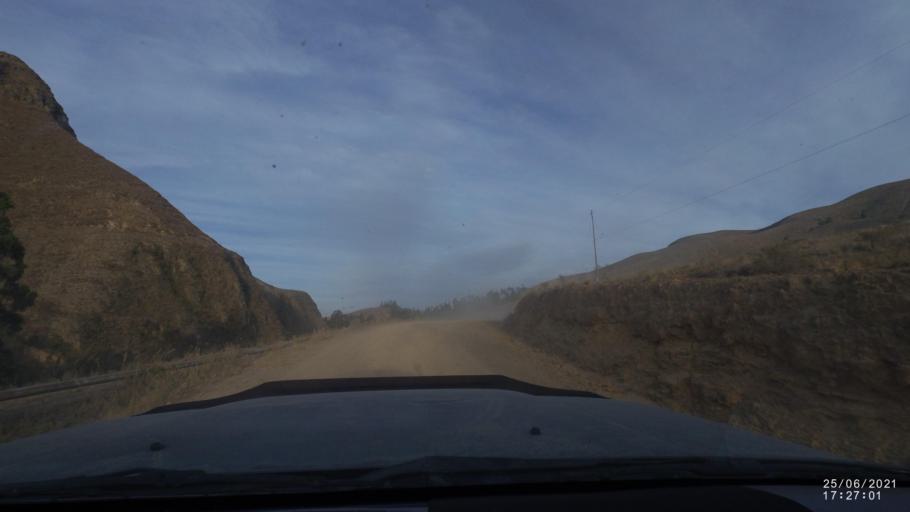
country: BO
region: Cochabamba
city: Mizque
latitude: -17.9211
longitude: -65.6782
